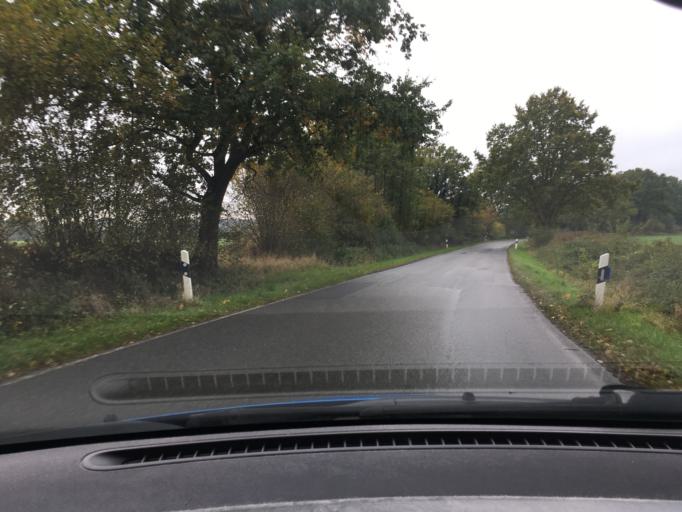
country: DE
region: Schleswig-Holstein
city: Nehmten
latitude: 54.0840
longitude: 10.4271
